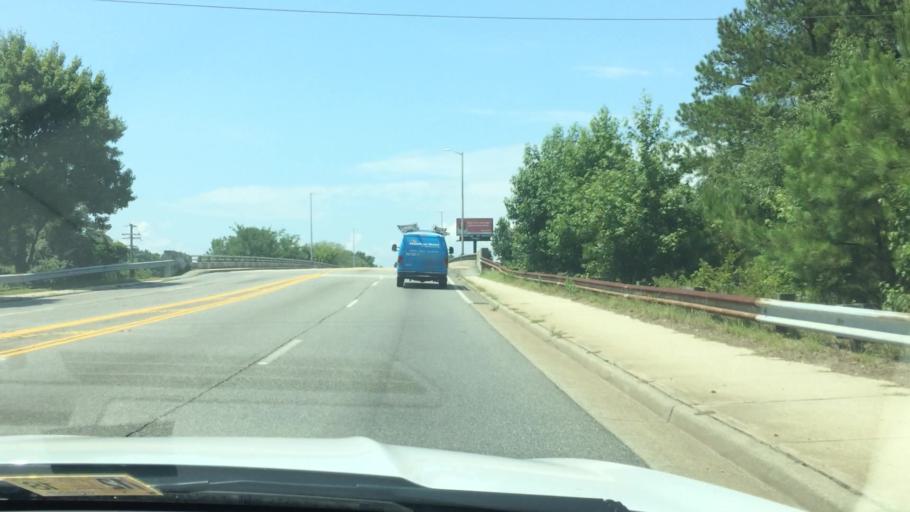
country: US
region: Virginia
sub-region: York County
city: Yorktown
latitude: 37.1359
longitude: -76.5252
